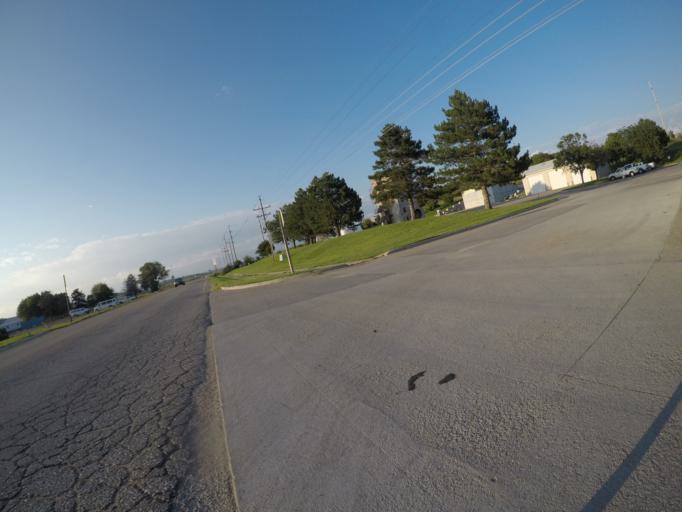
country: US
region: Kansas
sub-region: Riley County
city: Manhattan
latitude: 39.2053
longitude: -96.5854
